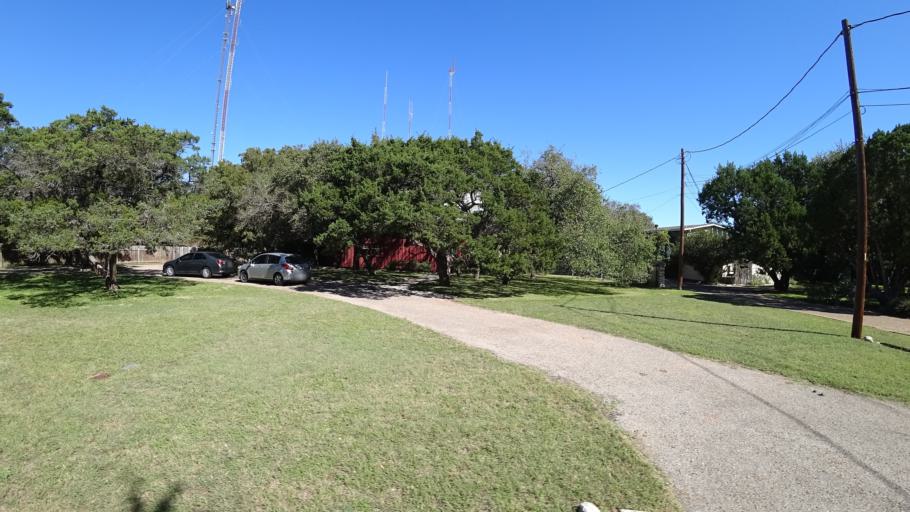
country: US
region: Texas
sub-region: Travis County
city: West Lake Hills
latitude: 30.3176
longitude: -97.8017
